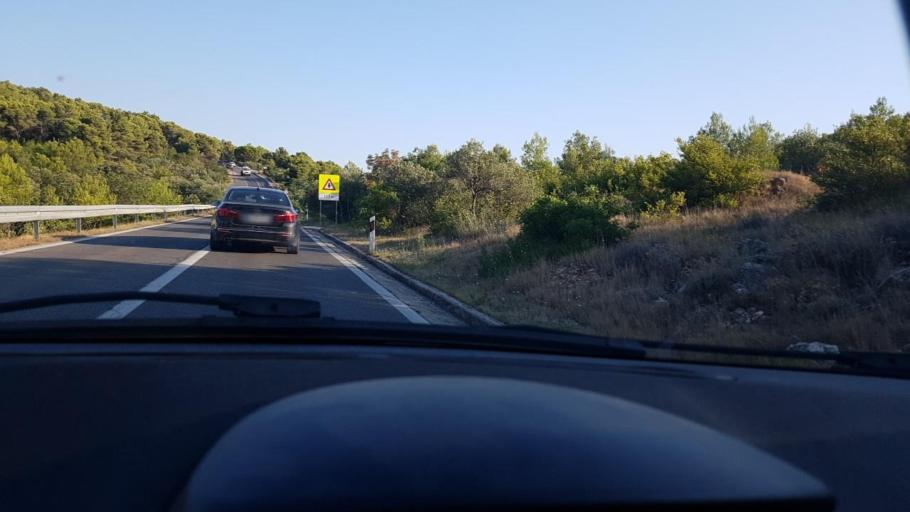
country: HR
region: Sibensko-Kniniska
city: Murter
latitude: 43.8023
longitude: 15.6113
